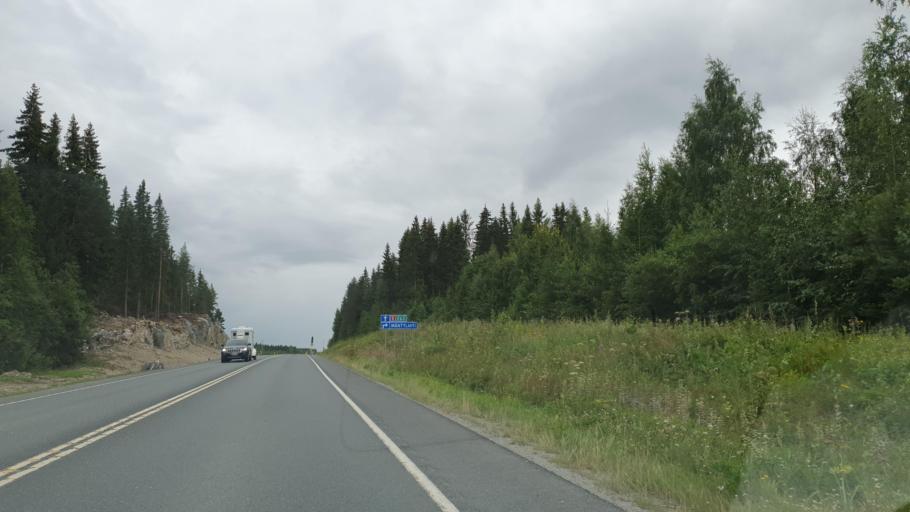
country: FI
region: Northern Savo
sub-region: Ylae-Savo
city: Lapinlahti
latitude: 63.3066
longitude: 27.4498
